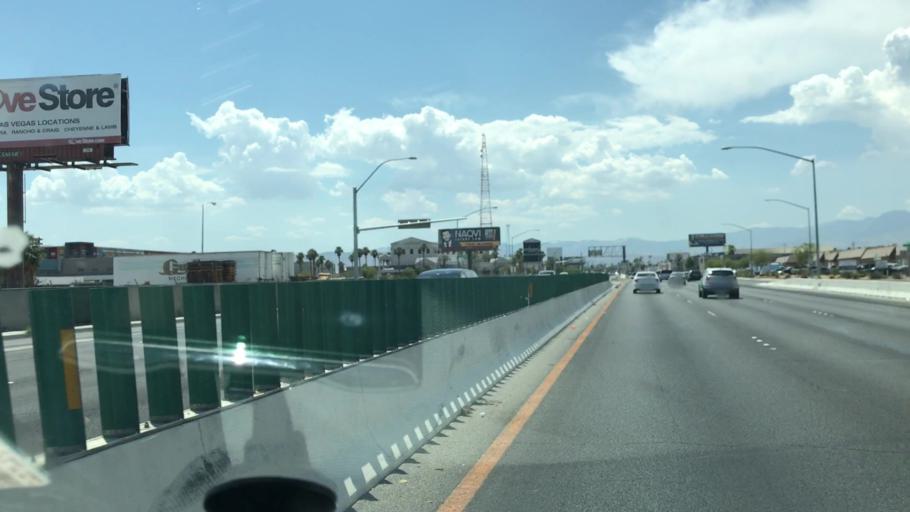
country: US
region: Nevada
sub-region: Clark County
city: Paradise
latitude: 36.1300
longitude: -115.1848
